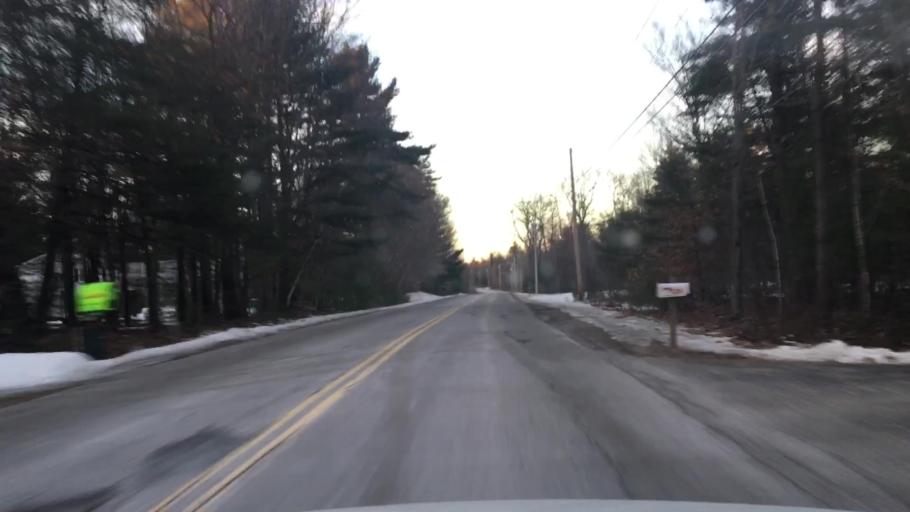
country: US
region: Maine
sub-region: York County
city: Lebanon
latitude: 43.3493
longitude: -70.8666
